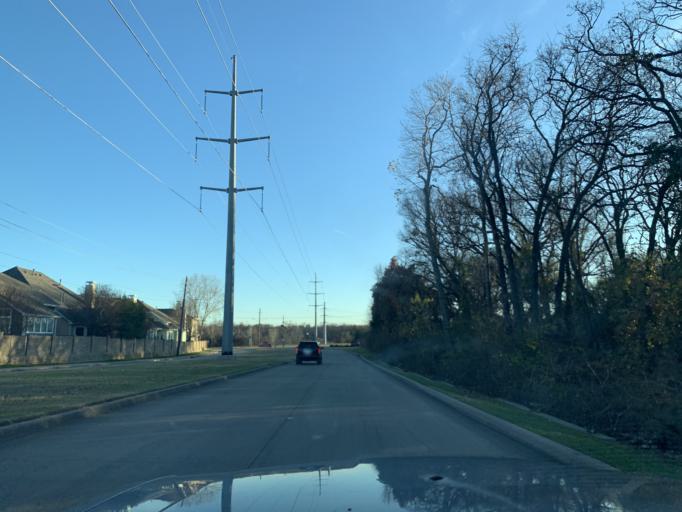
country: US
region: Texas
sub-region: Tarrant County
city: Euless
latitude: 32.8697
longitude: -97.0959
